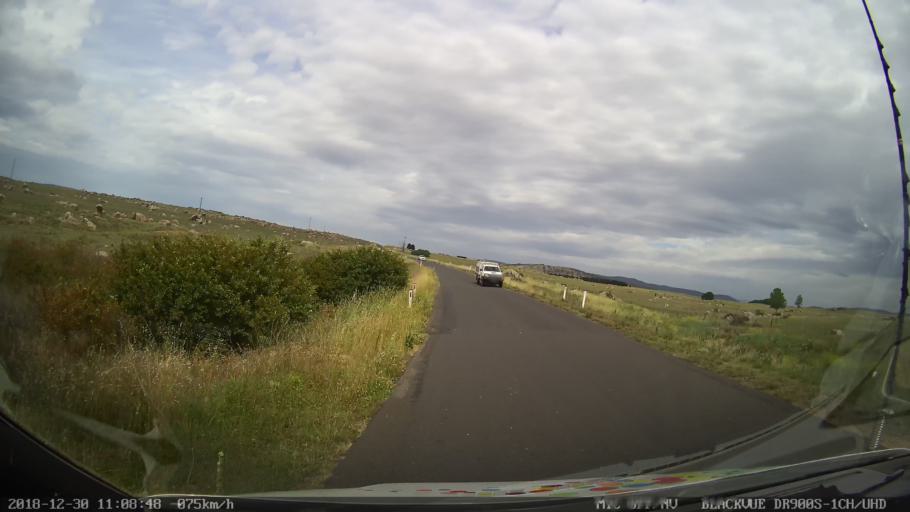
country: AU
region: New South Wales
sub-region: Snowy River
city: Berridale
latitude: -36.5041
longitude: 148.8019
